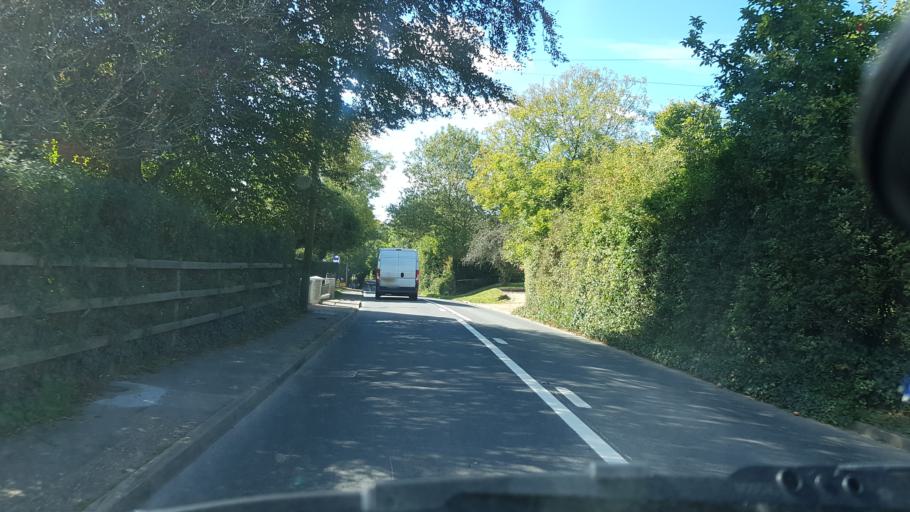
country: GB
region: England
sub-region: West Sussex
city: Billingshurst
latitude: 51.0227
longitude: -0.5080
